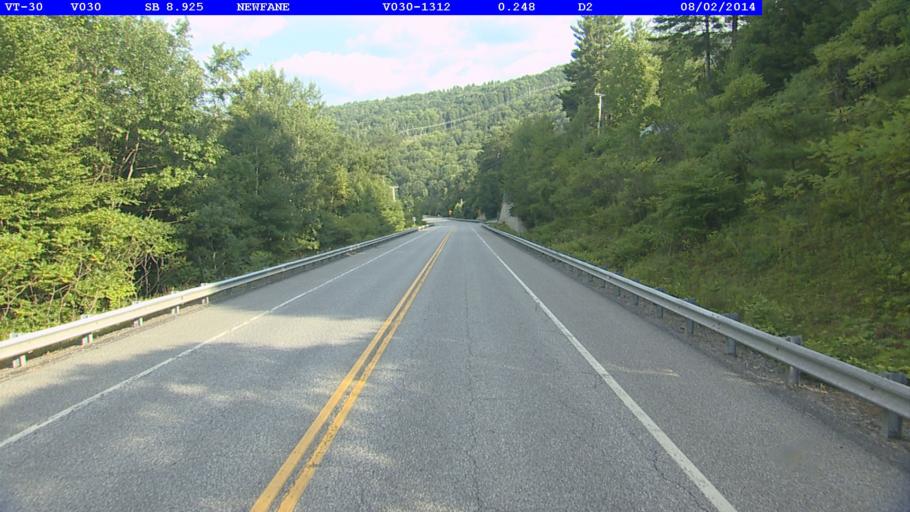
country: US
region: Vermont
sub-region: Windham County
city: Newfane
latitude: 42.9501
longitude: -72.6448
